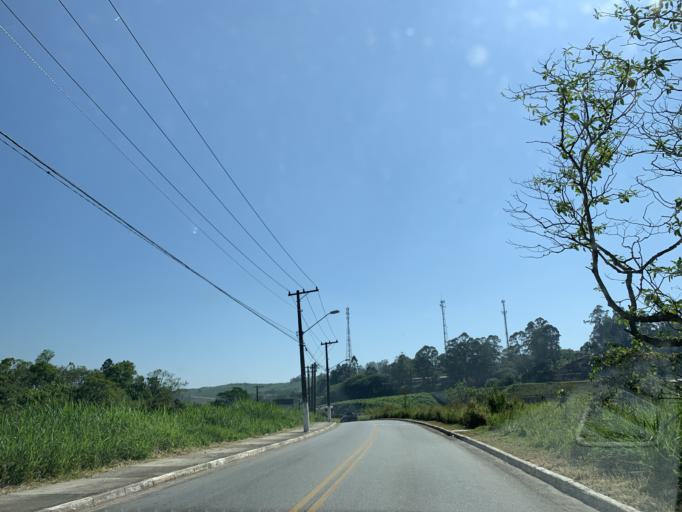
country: BR
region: Sao Paulo
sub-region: Caieiras
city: Caieiras
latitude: -23.4333
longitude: -46.7614
